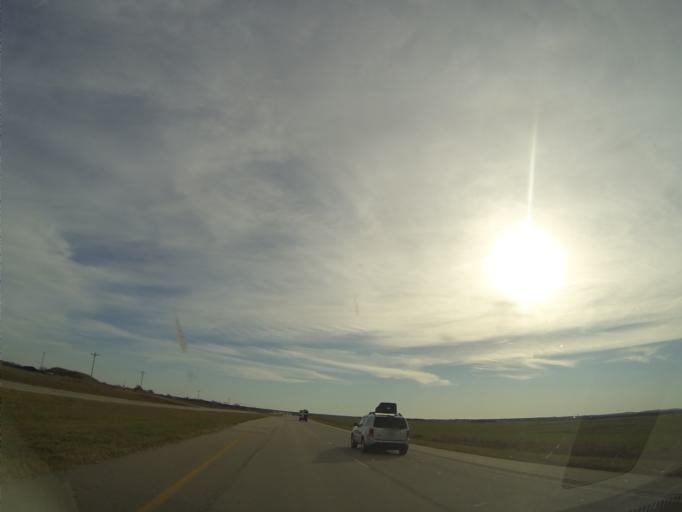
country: US
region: Kansas
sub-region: Ottawa County
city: Minneapolis
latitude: 39.1660
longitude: -97.6685
